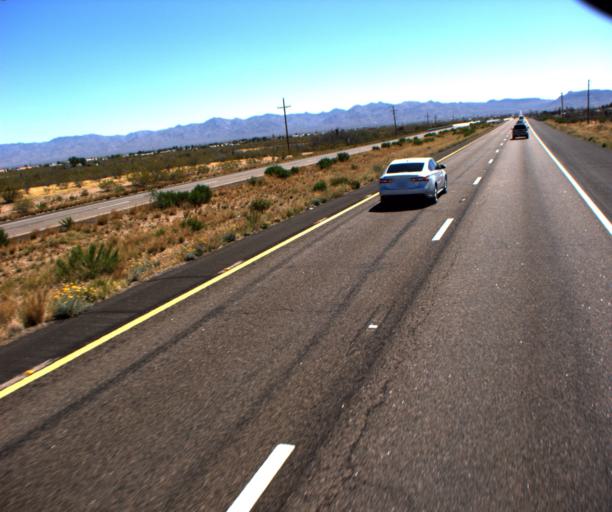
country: US
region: Arizona
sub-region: Mohave County
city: Golden Valley
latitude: 35.2253
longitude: -114.2868
